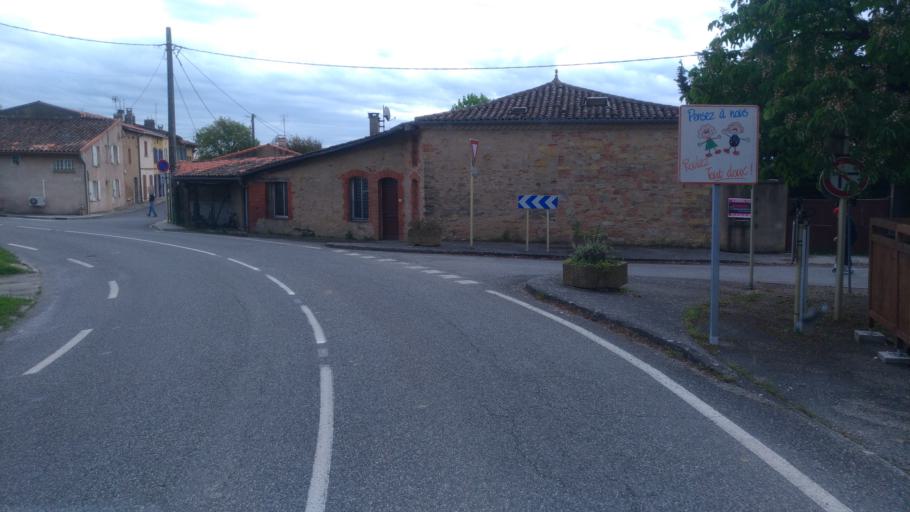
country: FR
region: Midi-Pyrenees
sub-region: Departement de la Haute-Garonne
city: Villefranche-de-Lauragais
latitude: 43.4245
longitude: 1.7555
